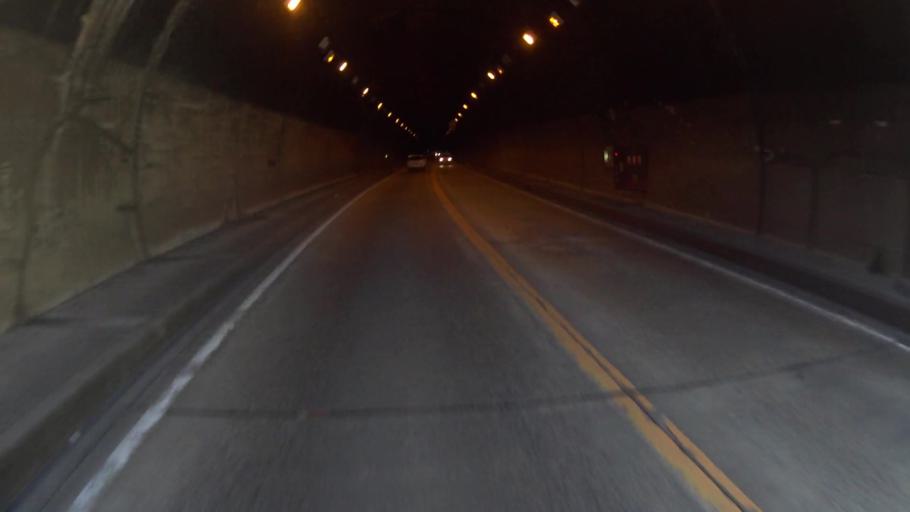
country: JP
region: Kyoto
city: Miyazu
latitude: 35.5471
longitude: 135.1832
